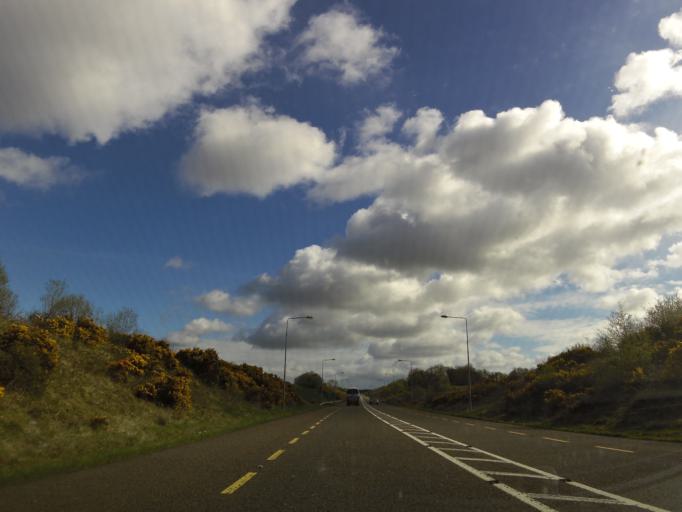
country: IE
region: Connaught
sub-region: Maigh Eo
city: Kiltamagh
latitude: 53.7991
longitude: -8.9215
